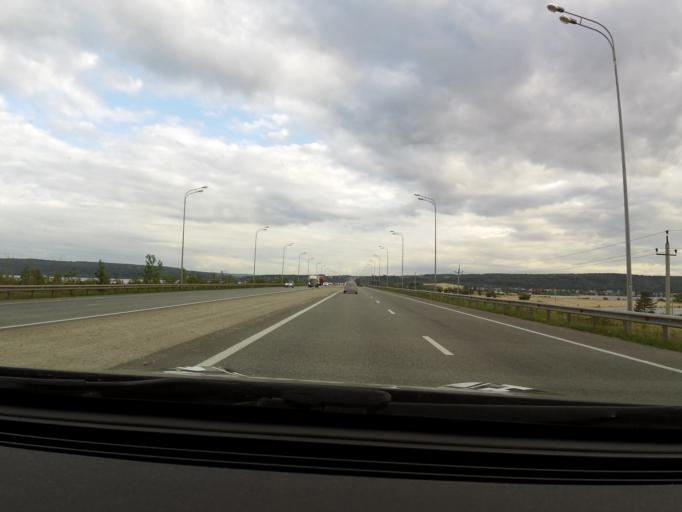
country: RU
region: Tatarstan
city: Osinovo
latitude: 55.8048
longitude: 48.8415
